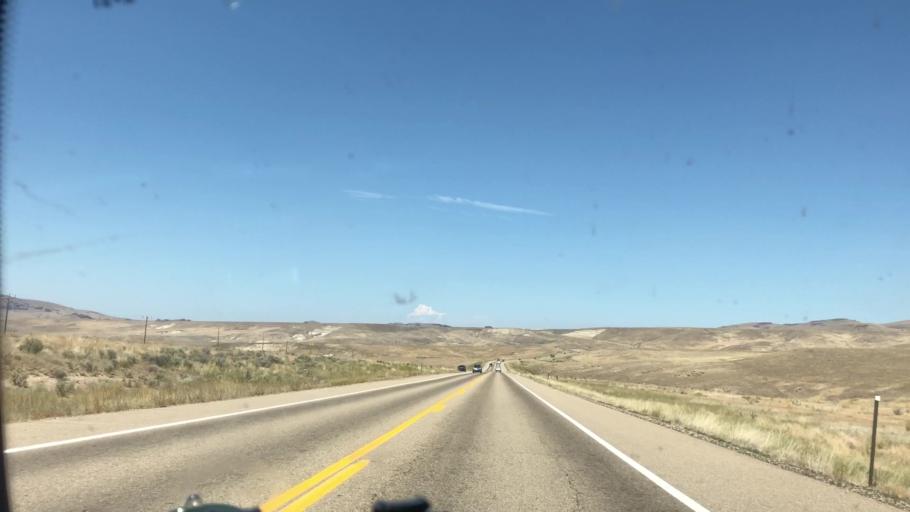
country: US
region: Idaho
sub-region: Owyhee County
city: Marsing
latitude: 43.2659
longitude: -117.0056
